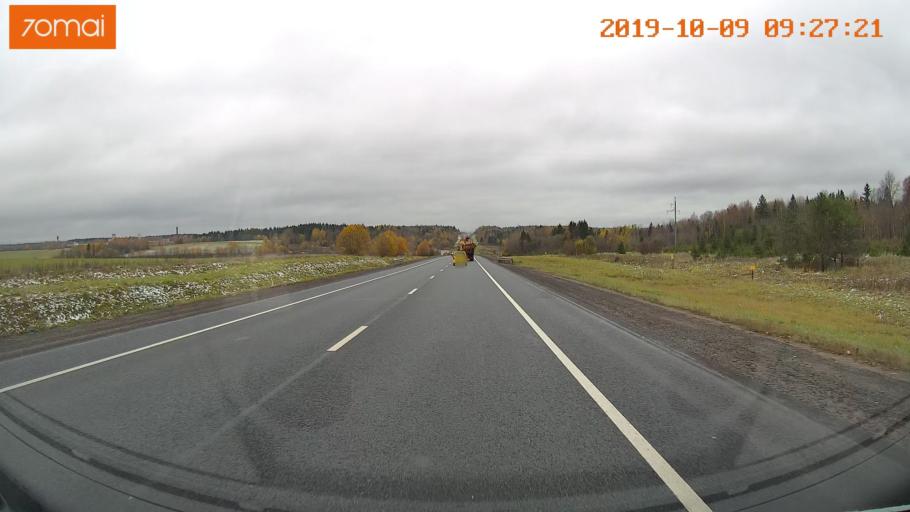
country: RU
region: Vologda
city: Vologda
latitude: 59.1118
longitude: 39.9796
